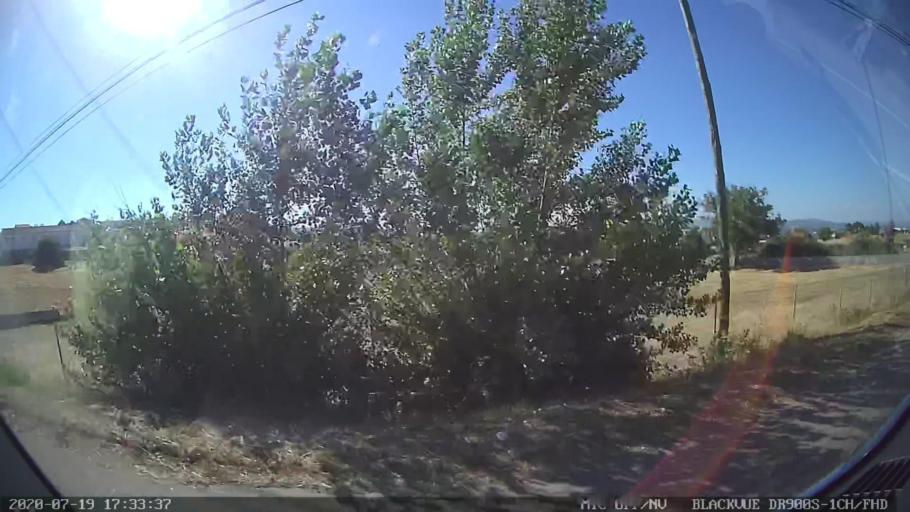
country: PT
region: Braganca
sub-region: Braganca Municipality
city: Braganca
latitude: 41.7758
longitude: -6.7855
